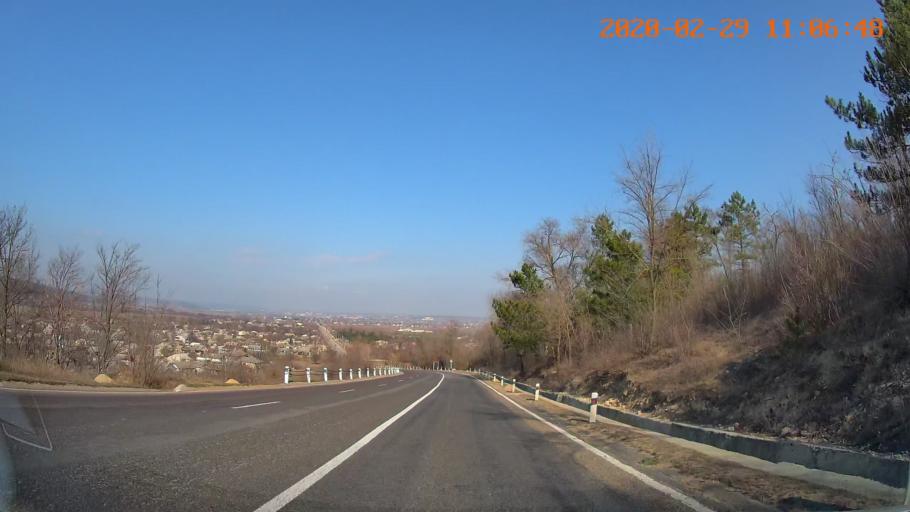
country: MD
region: Criuleni
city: Criuleni
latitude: 47.2186
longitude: 29.1866
